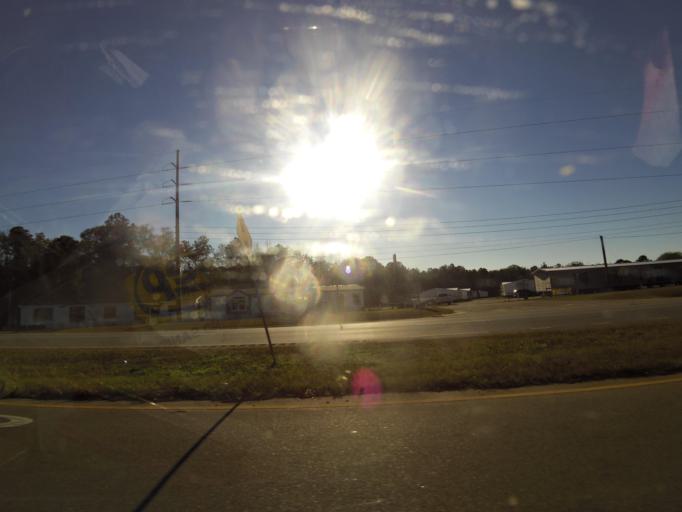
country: US
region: Alabama
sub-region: Houston County
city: Dothan
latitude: 31.1991
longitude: -85.4148
